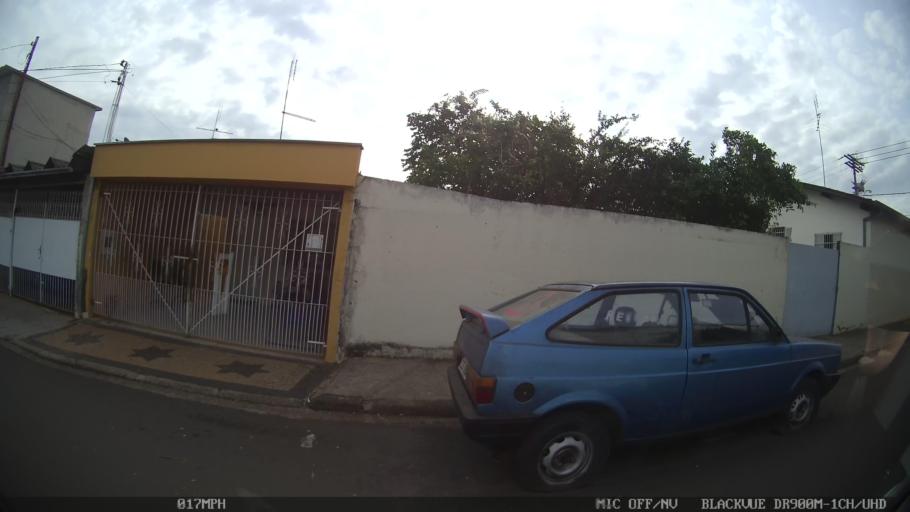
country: BR
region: Sao Paulo
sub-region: Piracicaba
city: Piracicaba
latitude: -22.7411
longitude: -47.6261
